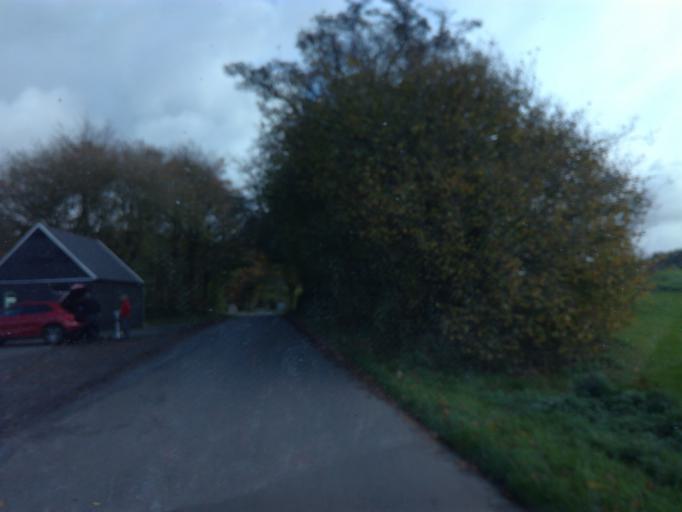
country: DK
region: South Denmark
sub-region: Vejle Kommune
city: Borkop
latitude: 55.6776
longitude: 9.6003
